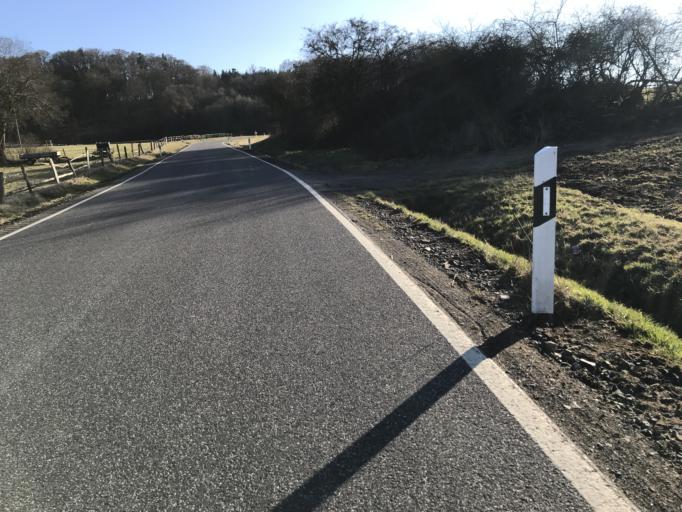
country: DE
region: Hesse
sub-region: Regierungsbezirk Giessen
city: Rabenau
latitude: 50.6692
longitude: 8.8564
